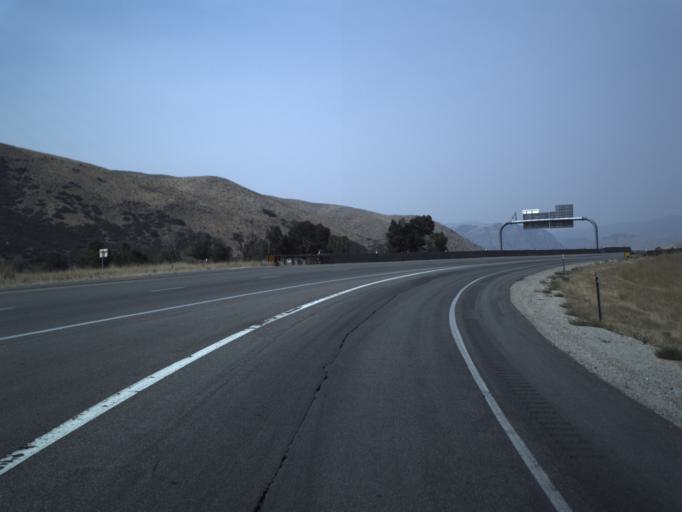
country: US
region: Utah
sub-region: Summit County
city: Coalville
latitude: 40.9718
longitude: -111.4419
